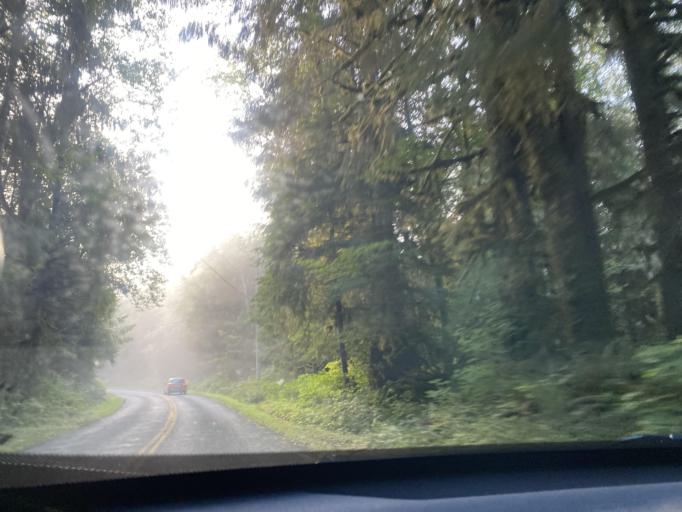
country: US
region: Washington
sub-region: Clallam County
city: Forks
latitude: 47.8085
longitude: -124.0953
